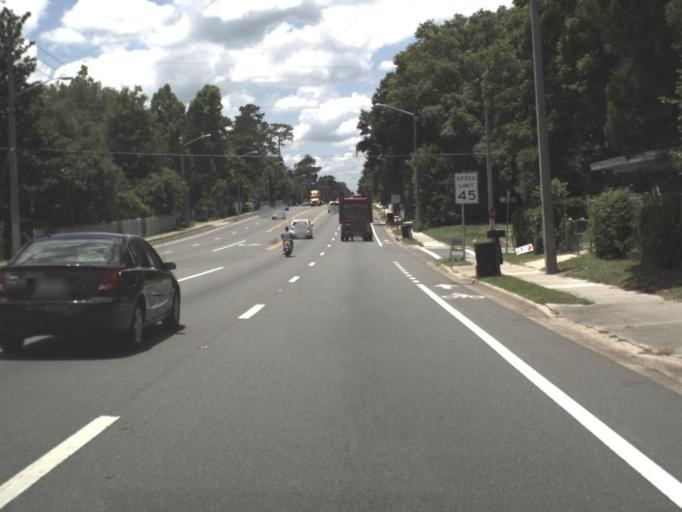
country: US
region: Florida
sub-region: Alachua County
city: Gainesville
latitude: 29.6886
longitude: -82.3341
